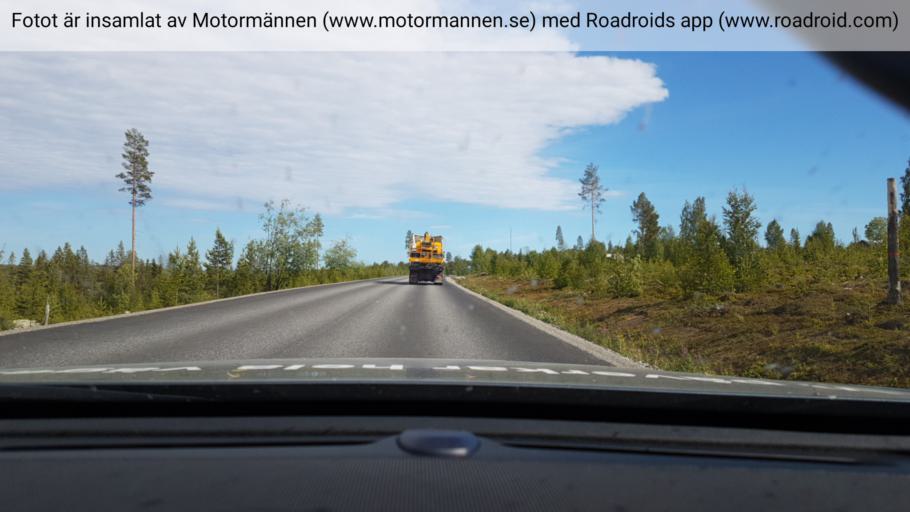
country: SE
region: Vaesterbotten
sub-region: Lycksele Kommun
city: Soderfors
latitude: 64.8374
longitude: 17.9922
